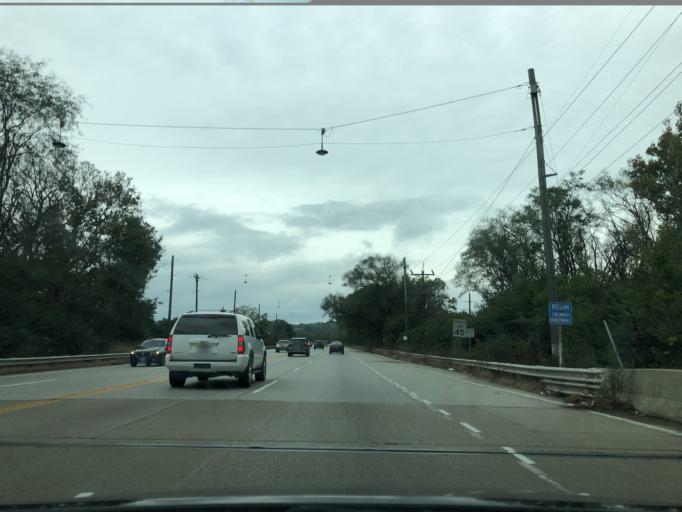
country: US
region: Ohio
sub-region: Hamilton County
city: Turpin Hills
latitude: 39.1096
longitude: -84.4018
